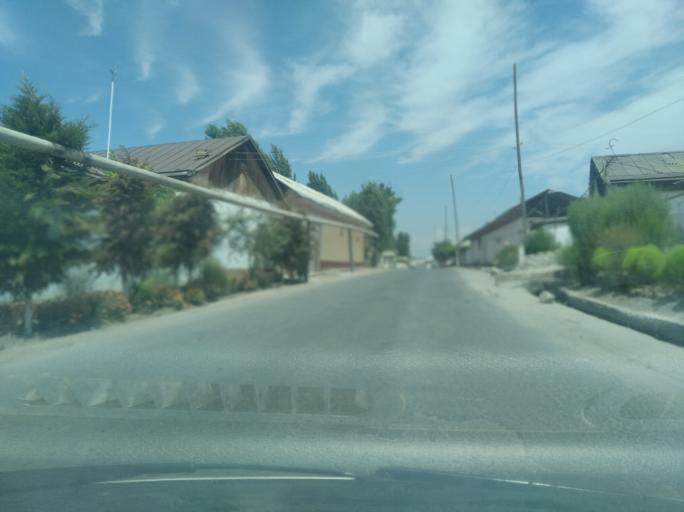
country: UZ
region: Andijon
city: Khujaobod
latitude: 40.6321
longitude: 72.4492
